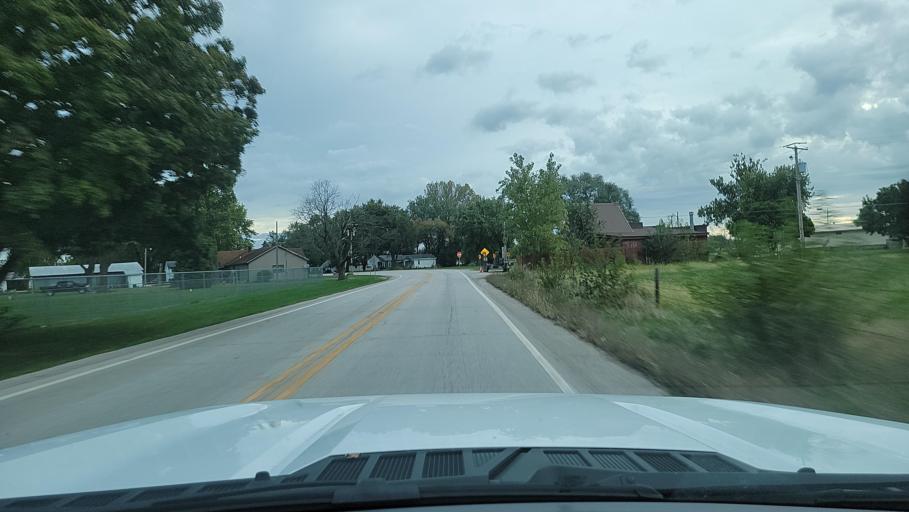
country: US
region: Illinois
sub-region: Schuyler County
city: Rushville
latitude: 40.1292
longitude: -90.5632
